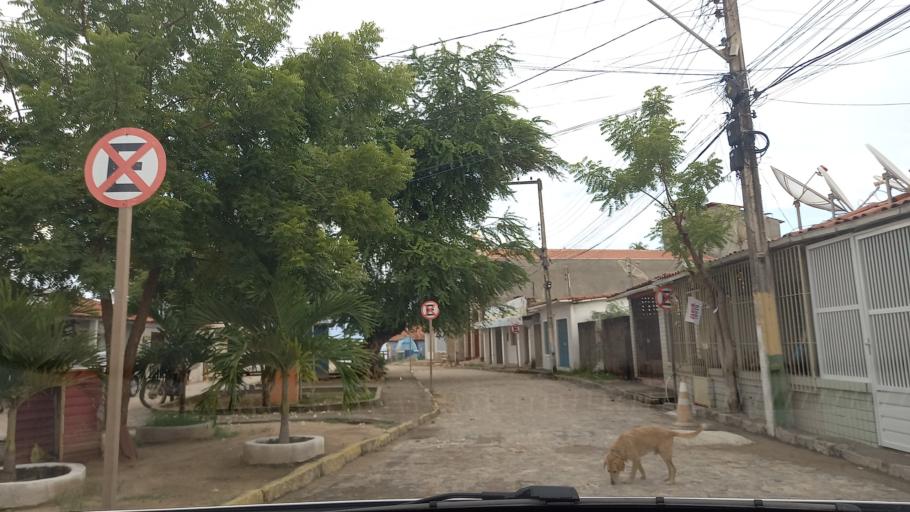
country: BR
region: Alagoas
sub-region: Maragogi
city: Maragogi
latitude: -8.9869
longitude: -35.1942
